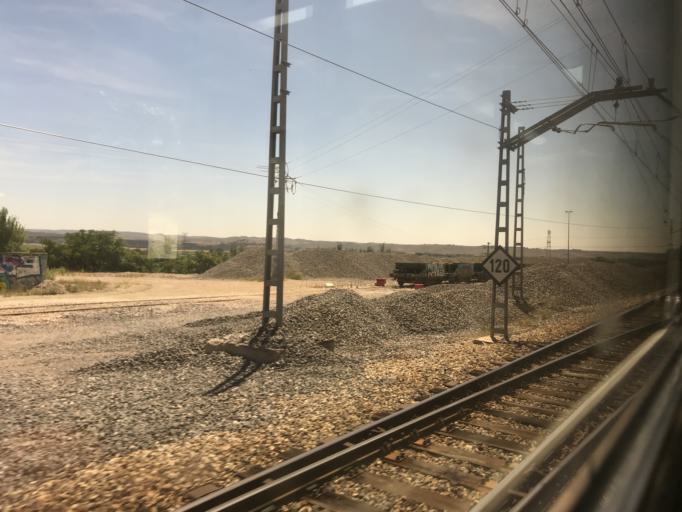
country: ES
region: Madrid
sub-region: Provincia de Madrid
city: Ciempozuelos
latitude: 40.1562
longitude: -3.6088
